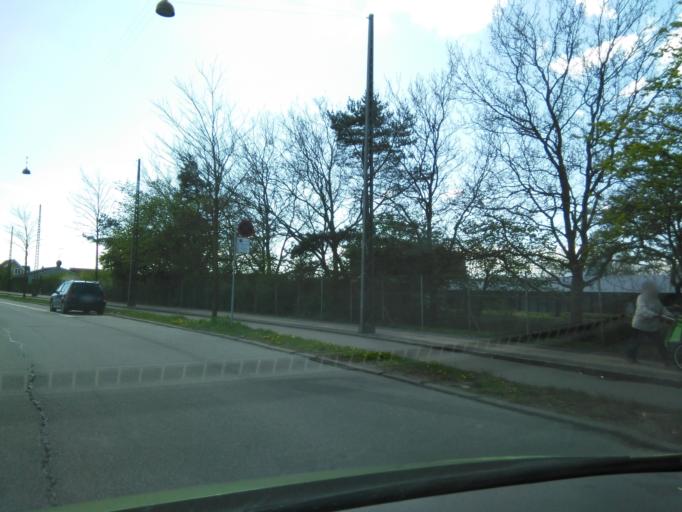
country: DK
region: Capital Region
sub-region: Tarnby Kommune
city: Tarnby
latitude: 55.6480
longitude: 12.5979
